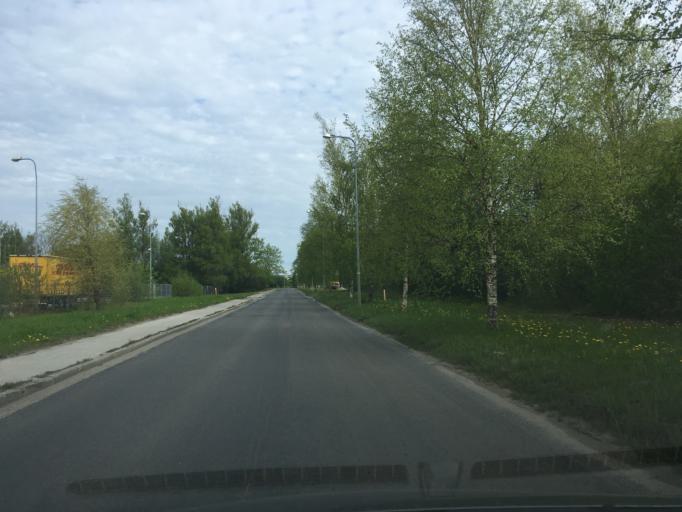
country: EE
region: Harju
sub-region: Tallinna linn
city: Kose
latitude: 59.4291
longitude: 24.8537
